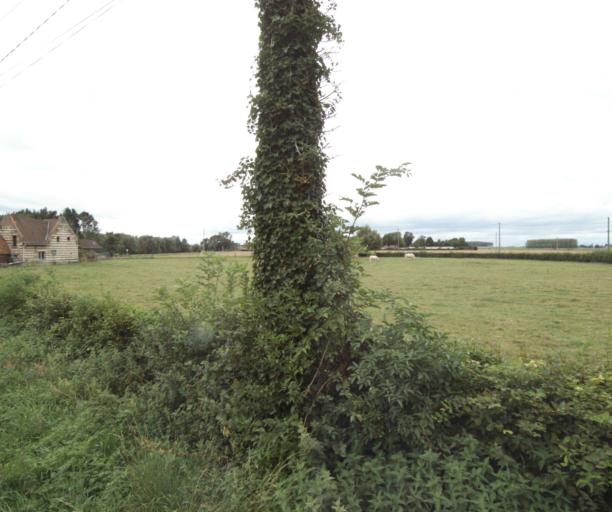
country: FR
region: Nord-Pas-de-Calais
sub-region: Departement du Nord
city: Sainghin-en-Melantois
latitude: 50.5675
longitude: 3.1809
